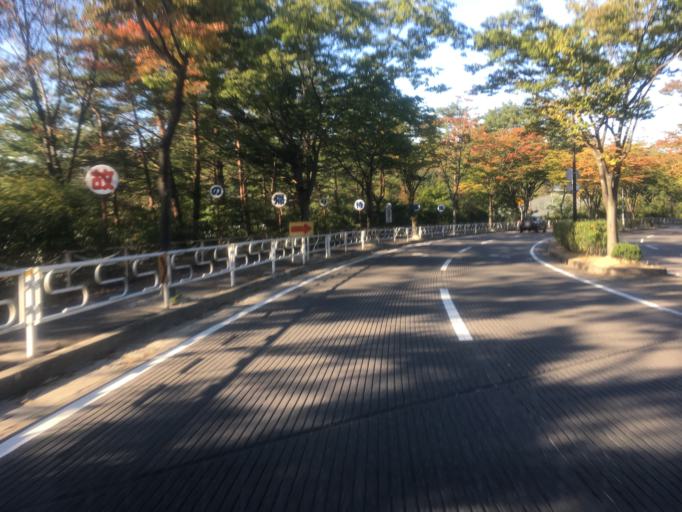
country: JP
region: Fukushima
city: Fukushima-shi
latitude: 37.7010
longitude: 140.4706
